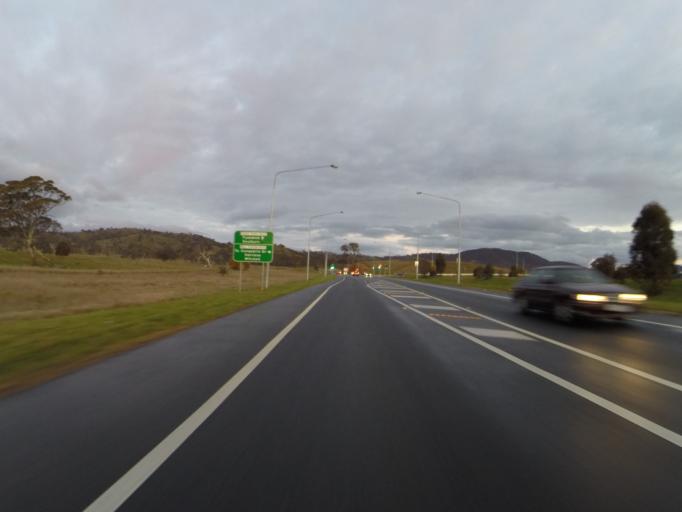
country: AU
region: Australian Capital Territory
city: Kaleen
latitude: -35.1992
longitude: 149.1642
